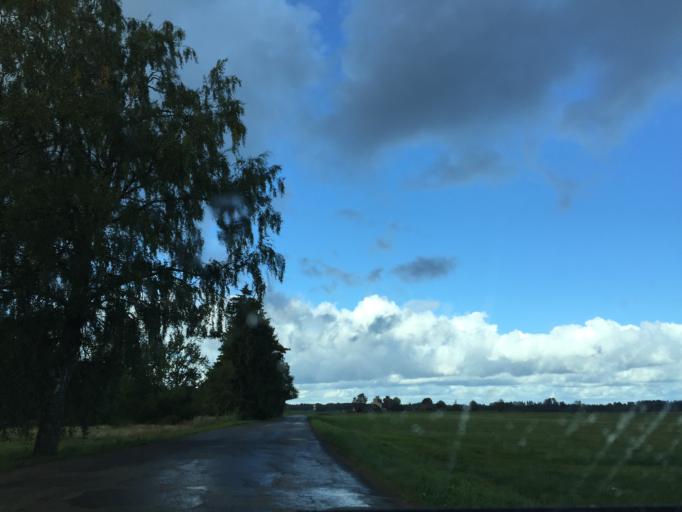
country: LV
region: Talsu Rajons
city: Sabile
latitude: 57.0523
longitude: 22.4710
